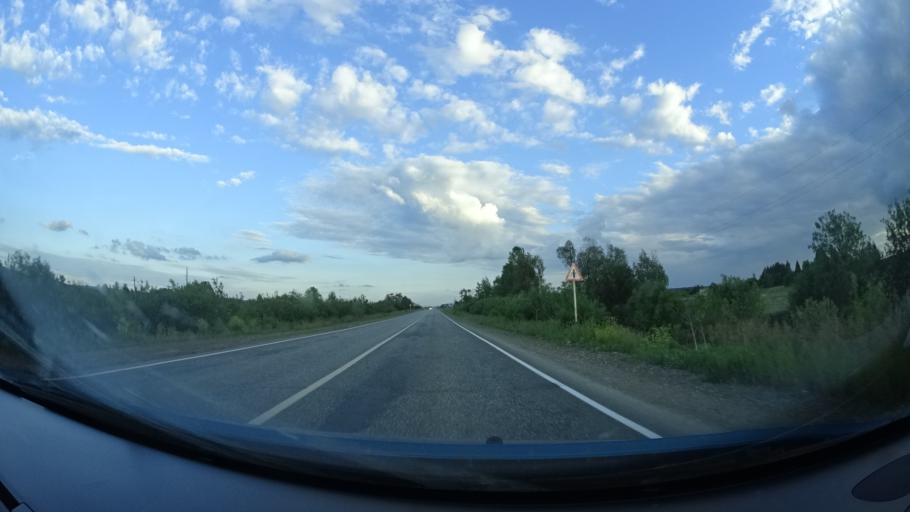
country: RU
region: Perm
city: Barda
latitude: 56.9708
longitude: 55.5780
